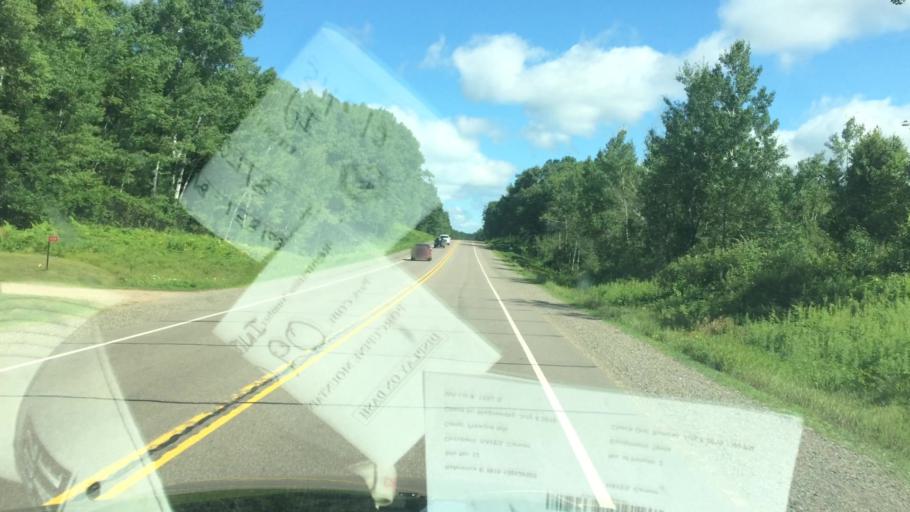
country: US
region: Wisconsin
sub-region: Oneida County
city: Rhinelander
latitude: 45.5779
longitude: -89.5693
